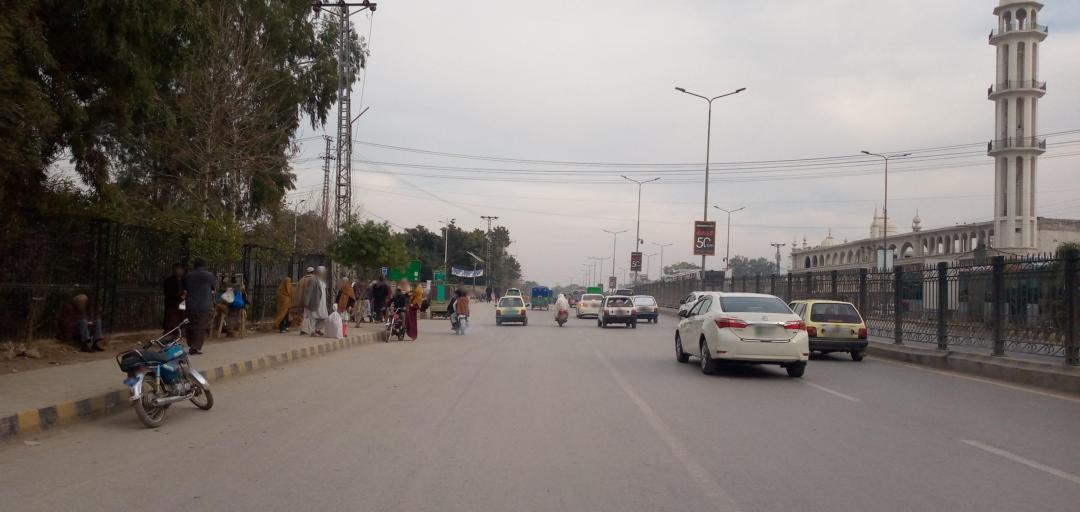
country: PK
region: Khyber Pakhtunkhwa
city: Peshawar
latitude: 33.9979
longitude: 71.4876
